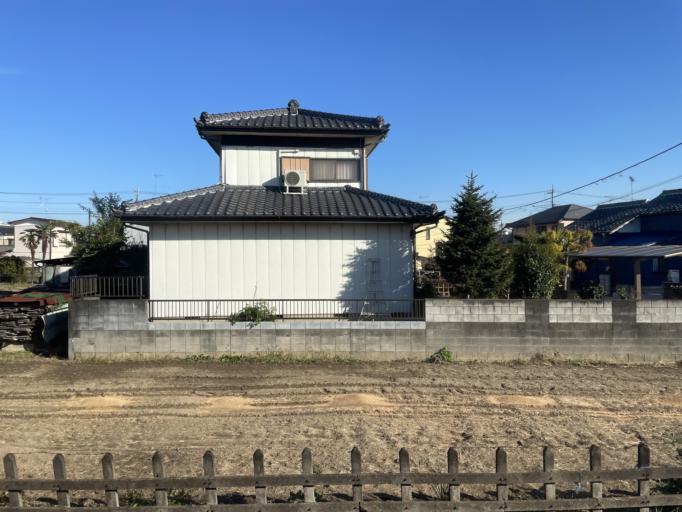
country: JP
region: Saitama
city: Satte
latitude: 36.0813
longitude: 139.7157
